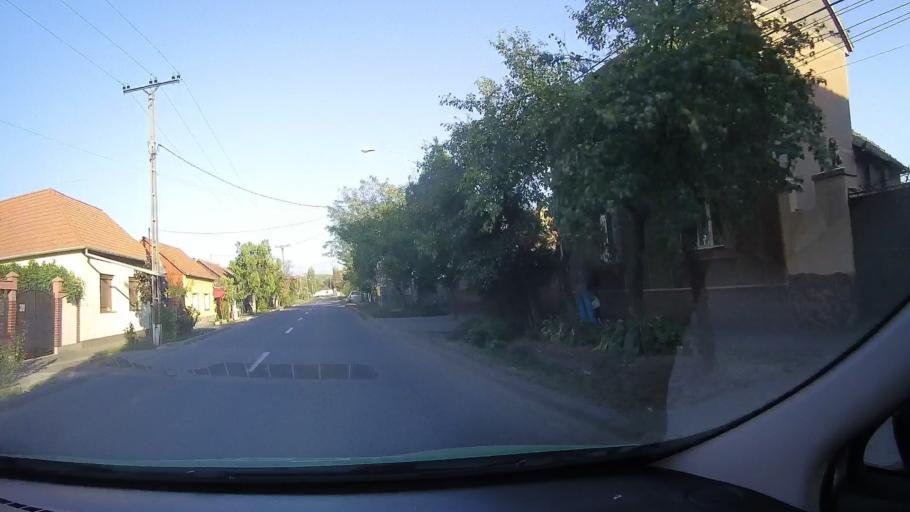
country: RO
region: Bihor
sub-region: Comuna Santandrei
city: Santandrei
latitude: 47.1035
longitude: 21.8902
